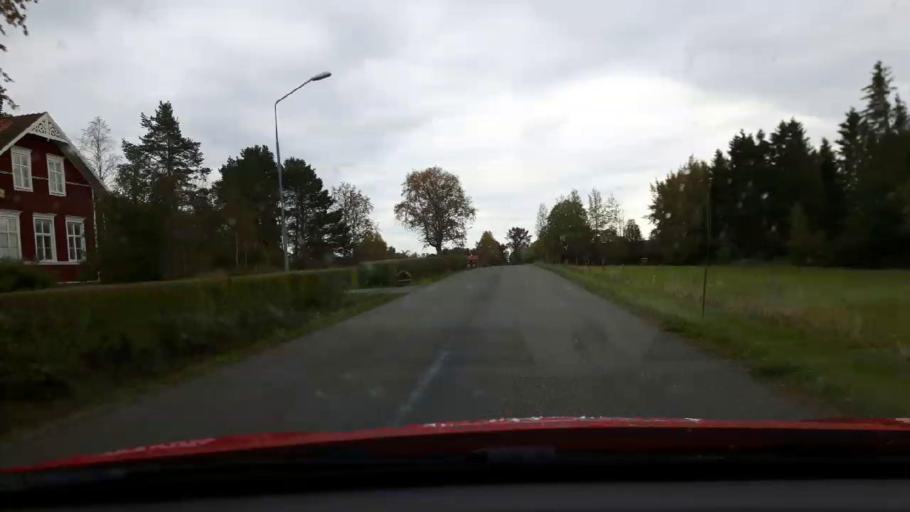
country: SE
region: Jaemtland
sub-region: Bergs Kommun
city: Hoverberg
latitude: 62.9599
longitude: 14.4900
